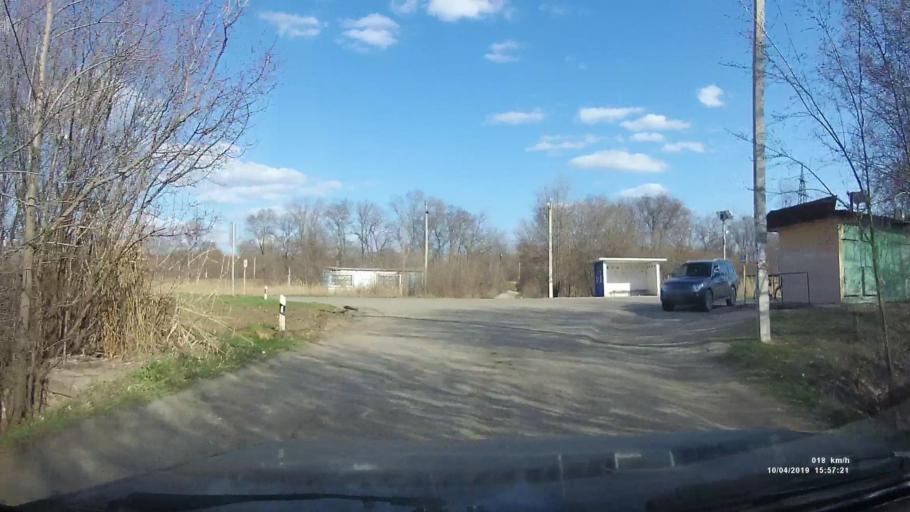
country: RU
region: Rostov
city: Masalovka
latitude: 48.4101
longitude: 40.2751
